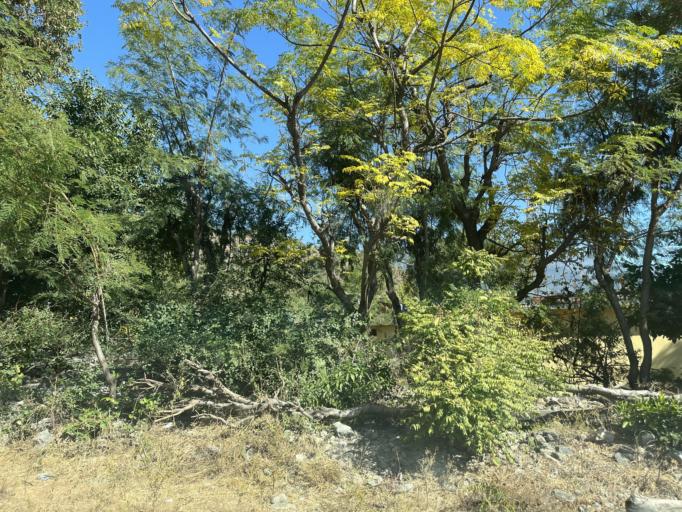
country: IN
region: Uttarakhand
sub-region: Almora
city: Ranikhet
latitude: 29.5553
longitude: 79.3401
